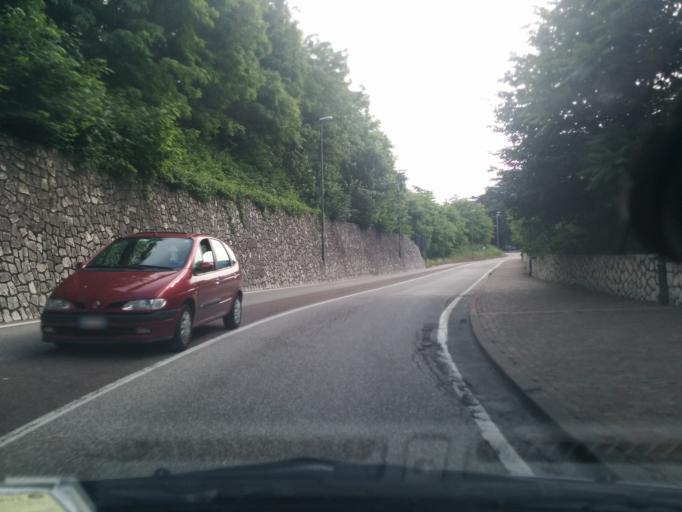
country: IT
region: Trentino-Alto Adige
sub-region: Provincia di Trento
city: Povo
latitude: 46.0685
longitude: 11.1405
